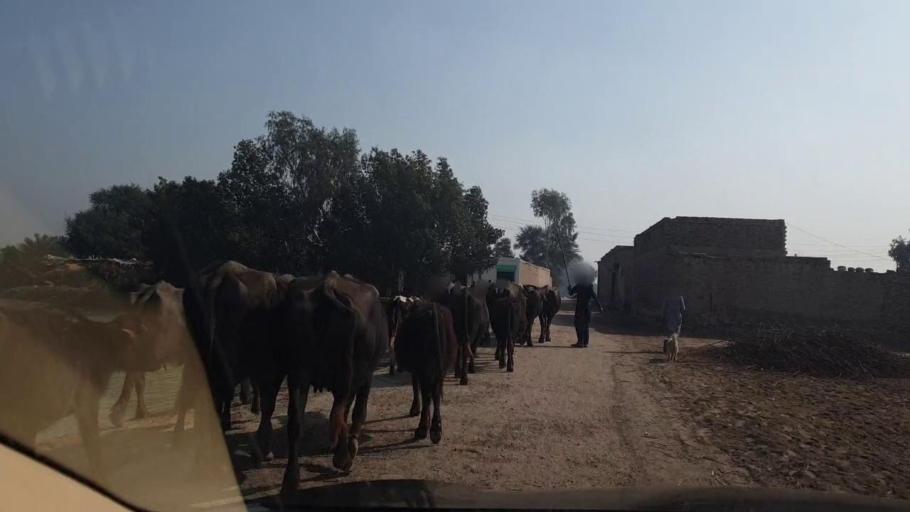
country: PK
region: Sindh
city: Ubauro
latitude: 28.1154
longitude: 69.7243
